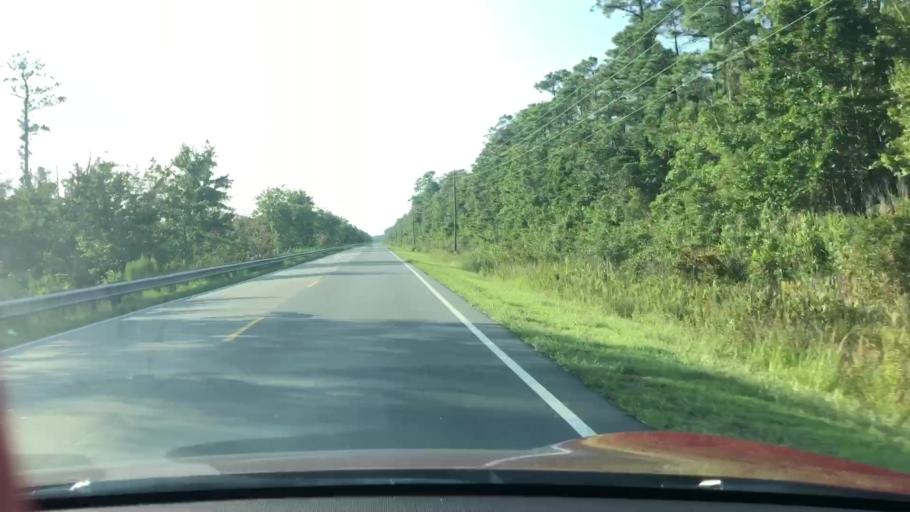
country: US
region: North Carolina
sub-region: Dare County
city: Manteo
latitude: 35.8181
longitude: -75.7977
